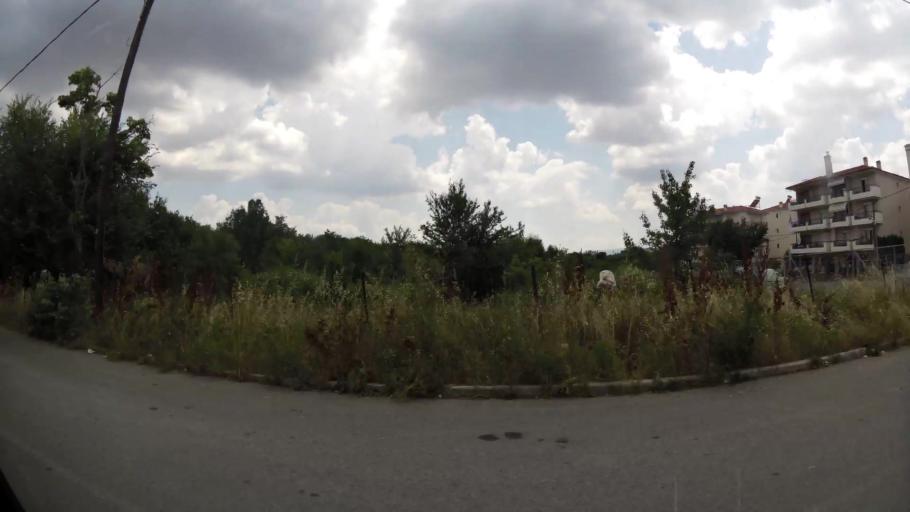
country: GR
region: West Macedonia
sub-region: Nomos Kozanis
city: Kozani
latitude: 40.2995
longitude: 21.8041
